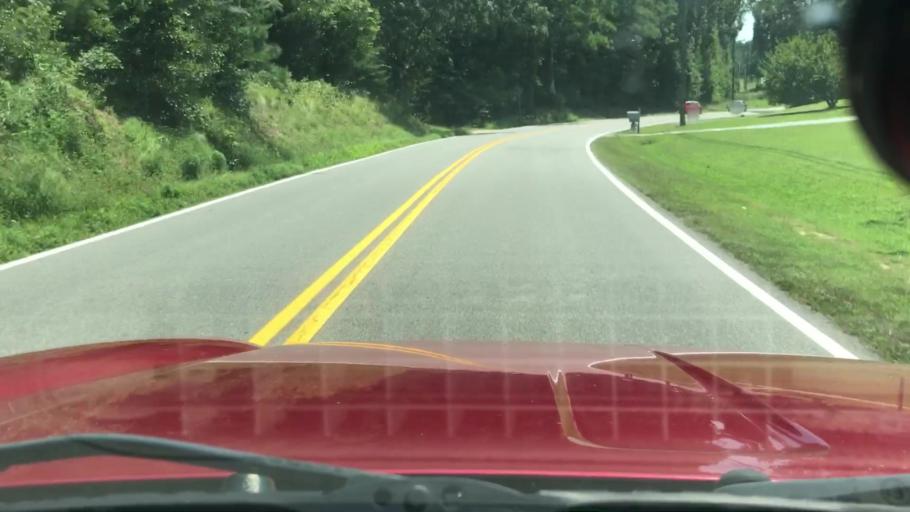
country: US
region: Virginia
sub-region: Chesterfield County
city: Chester
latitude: 37.3188
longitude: -77.4166
